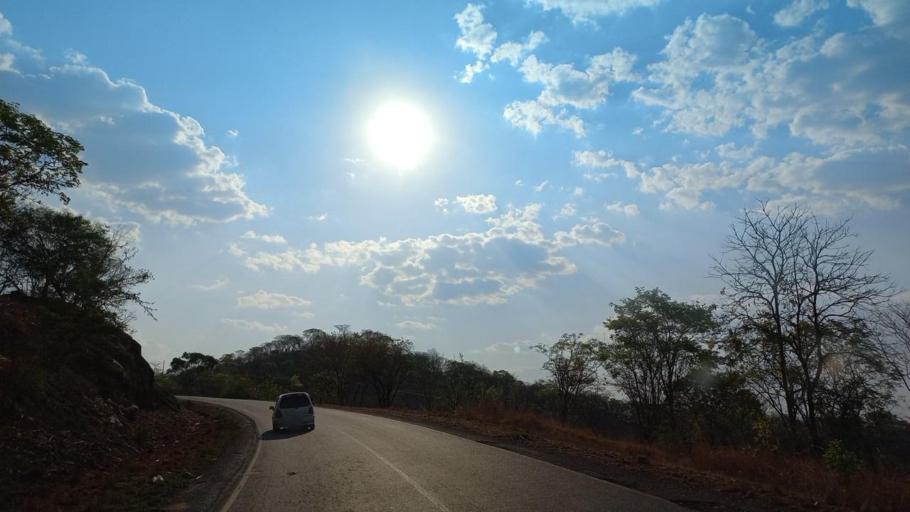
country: ZM
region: Lusaka
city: Luangwa
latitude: -14.9726
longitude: 30.0085
